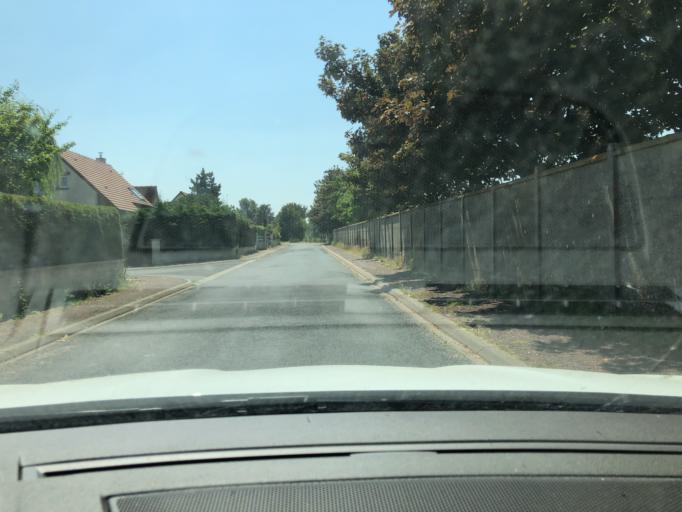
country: FR
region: Lower Normandy
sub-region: Departement du Calvados
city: Lion-sur-Mer
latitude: 49.3001
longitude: -0.3245
